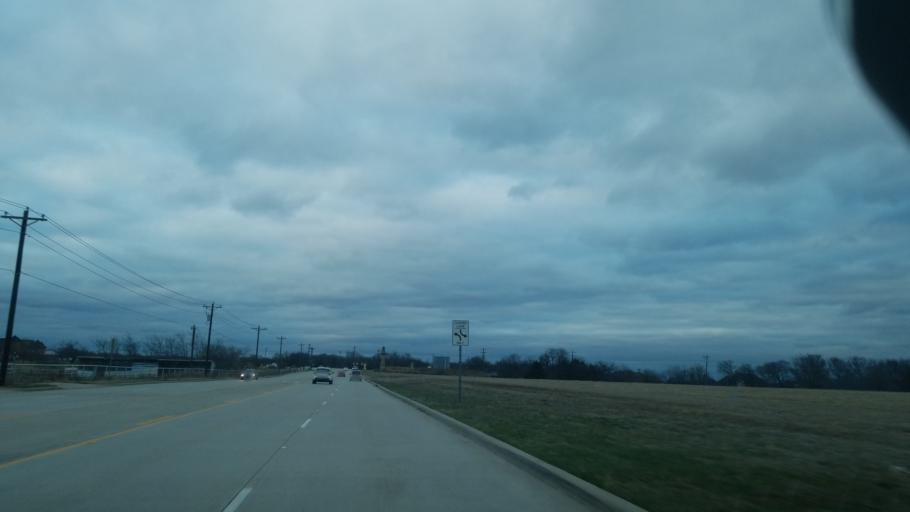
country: US
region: Texas
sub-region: Denton County
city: Little Elm
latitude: 33.1454
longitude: -96.9746
